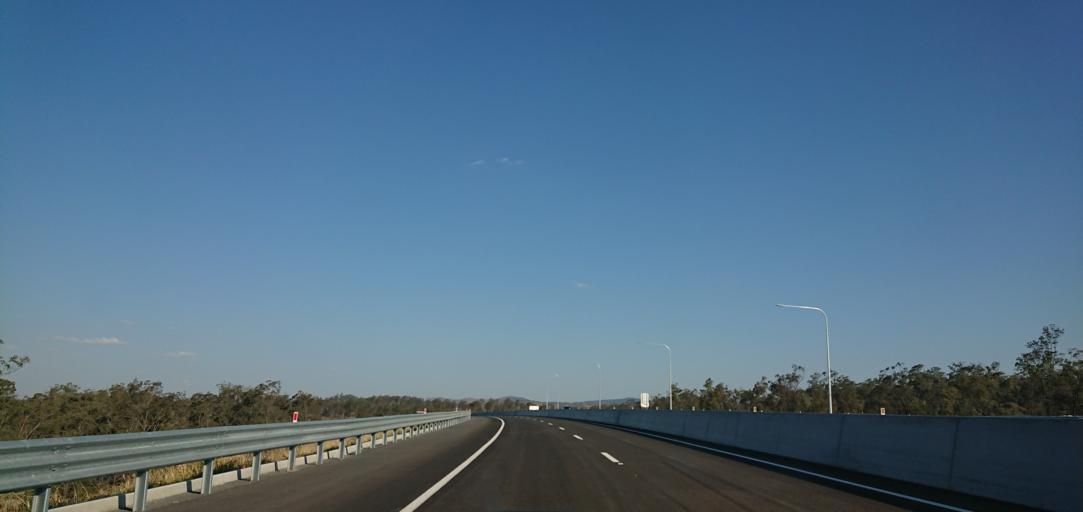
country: AU
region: Queensland
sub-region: Toowoomba
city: Rangeville
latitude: -27.5419
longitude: 152.0783
